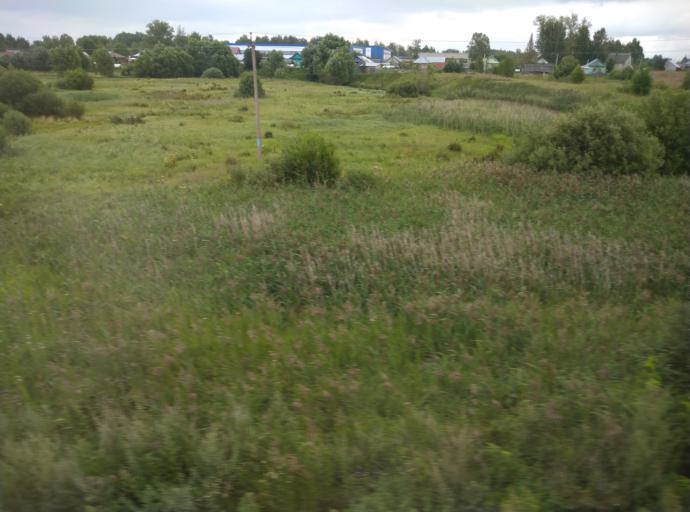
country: RU
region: Kostroma
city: Nerekhta
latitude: 57.4720
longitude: 40.5725
